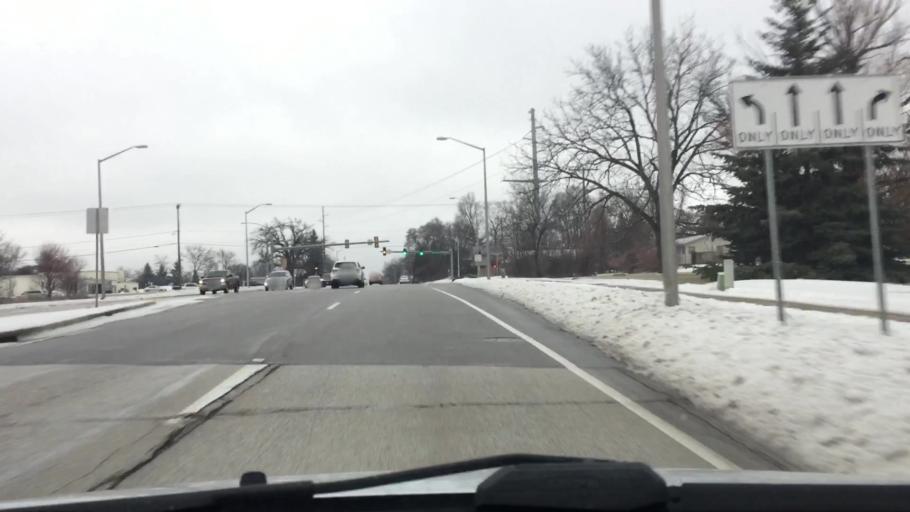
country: US
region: Wisconsin
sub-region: Waukesha County
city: Waukesha
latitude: 43.0335
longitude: -88.2560
